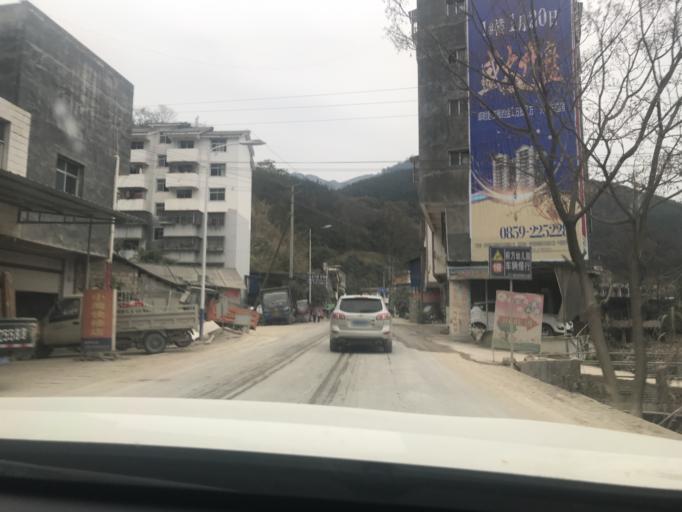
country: CN
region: Guangxi Zhuangzu Zizhiqu
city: Xinzhou
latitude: 24.9829
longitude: 105.8188
